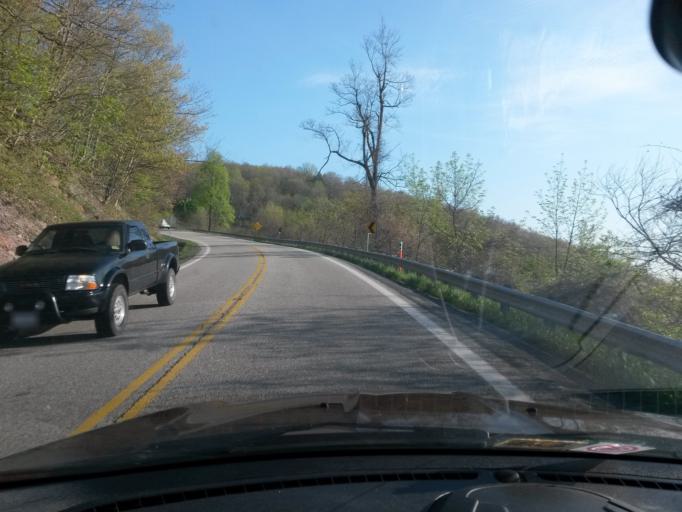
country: US
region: Virginia
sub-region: Bath County
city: Warm Springs
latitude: 38.0492
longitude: -79.7657
